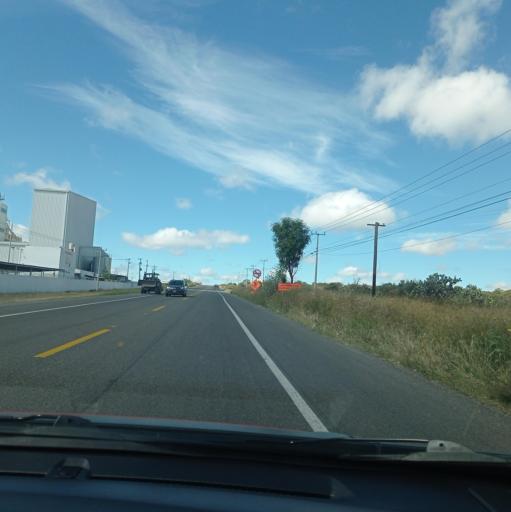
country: MX
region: Jalisco
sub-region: San Julian
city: Colonia Veintitres de Mayo
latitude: 21.0120
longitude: -102.2158
